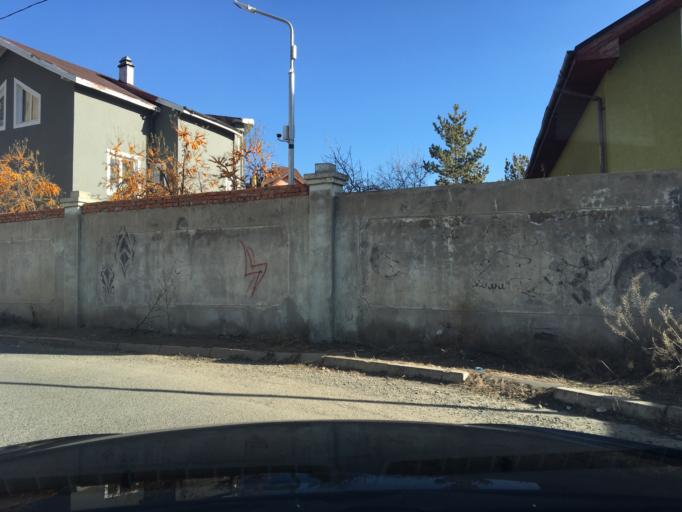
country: MN
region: Ulaanbaatar
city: Ulaanbaatar
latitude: 47.8912
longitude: 106.9066
